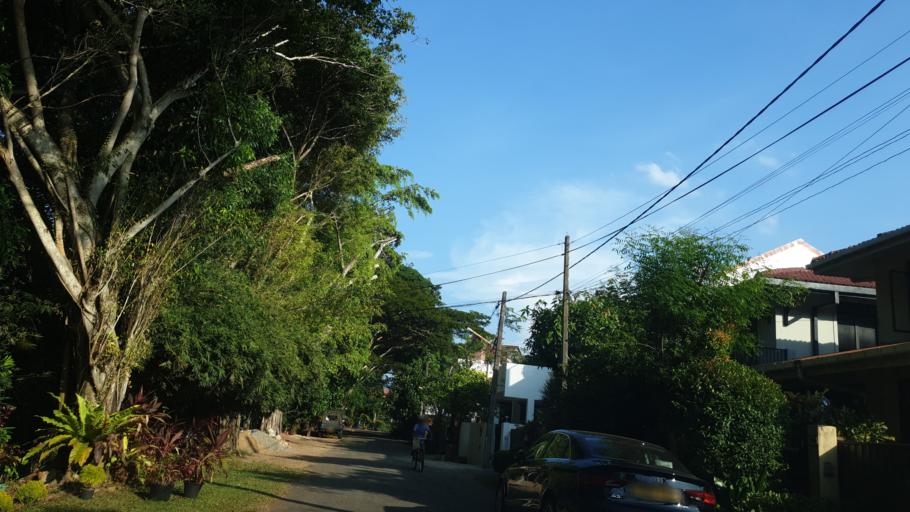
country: LK
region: Western
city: Galkissa
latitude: 6.8457
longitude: 79.8800
